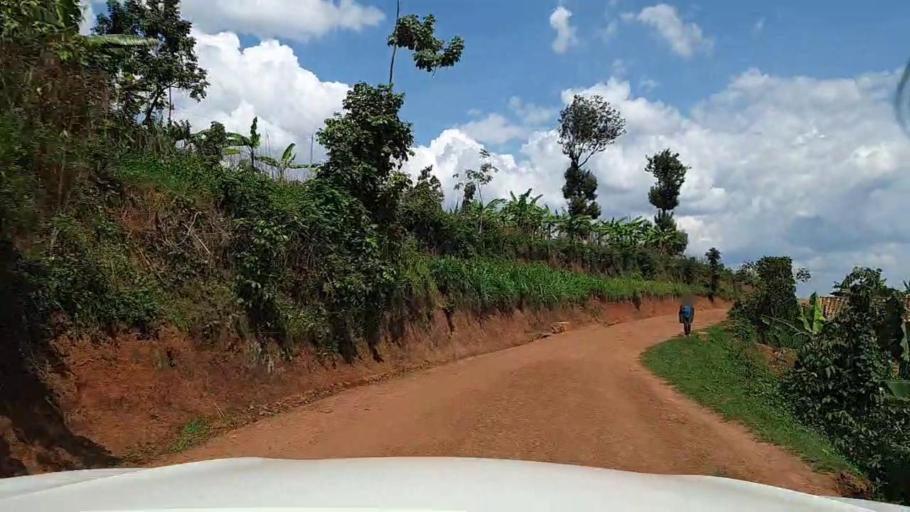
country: RW
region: Southern Province
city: Butare
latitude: -2.7471
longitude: 29.7051
